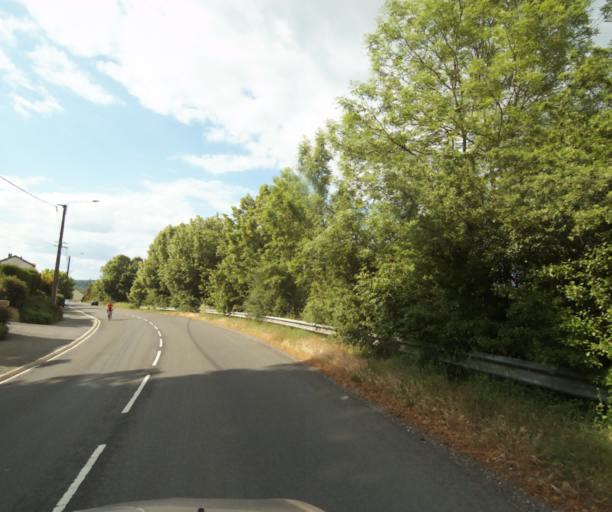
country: FR
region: Champagne-Ardenne
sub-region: Departement des Ardennes
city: Montcy-Notre-Dame
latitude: 49.7674
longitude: 4.7436
